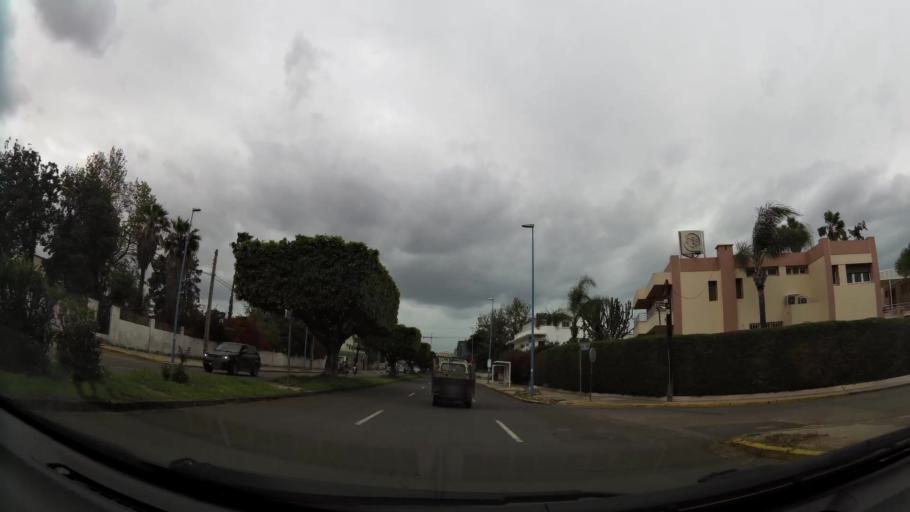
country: MA
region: Grand Casablanca
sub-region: Casablanca
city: Casablanca
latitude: 33.5623
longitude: -7.6424
